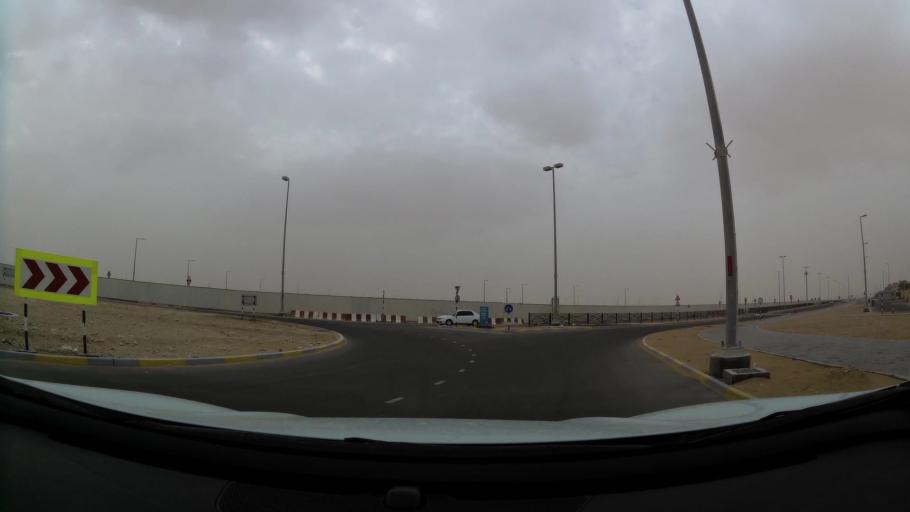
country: AE
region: Abu Dhabi
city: Abu Dhabi
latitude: 24.4420
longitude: 54.7208
